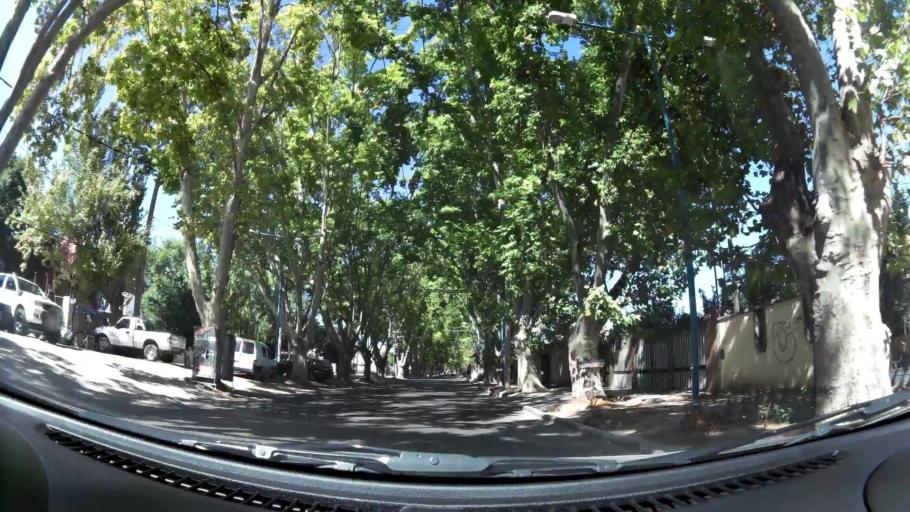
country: AR
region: Mendoza
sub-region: Departamento de Godoy Cruz
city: Godoy Cruz
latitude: -32.9452
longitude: -68.8423
